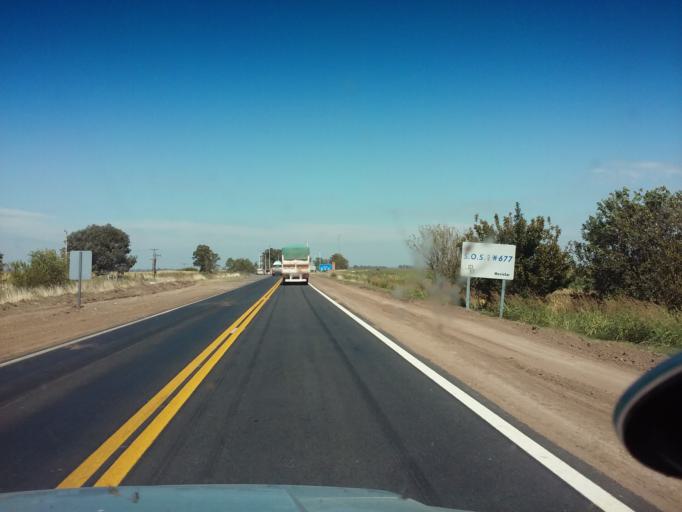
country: AR
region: Buenos Aires
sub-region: Partido de Nueve de Julio
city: Nueve de Julio
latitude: -35.3574
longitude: -60.6994
